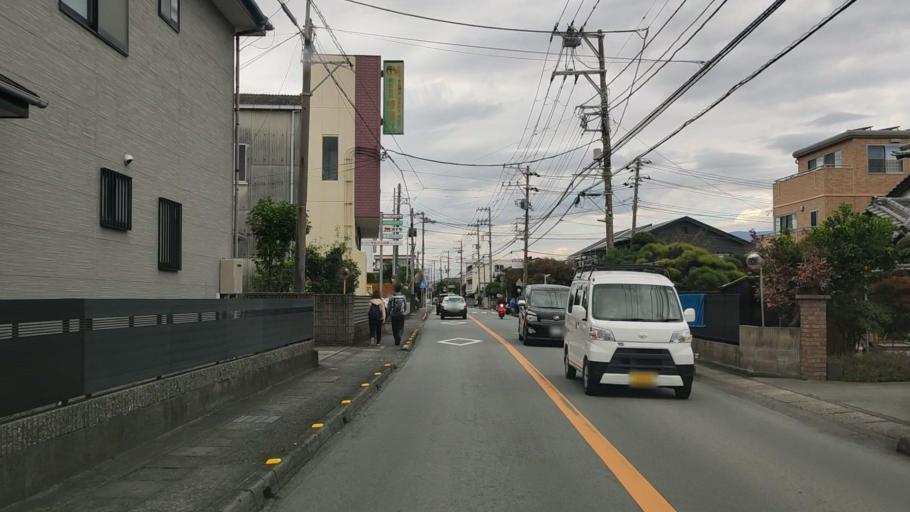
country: JP
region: Shizuoka
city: Numazu
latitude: 35.1045
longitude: 138.8391
